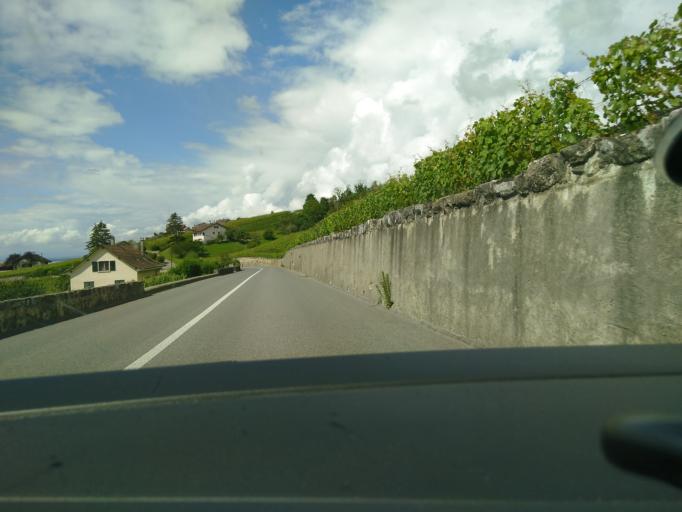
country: CH
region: Vaud
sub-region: Morges District
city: Aubonne
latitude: 46.4854
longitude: 6.3768
